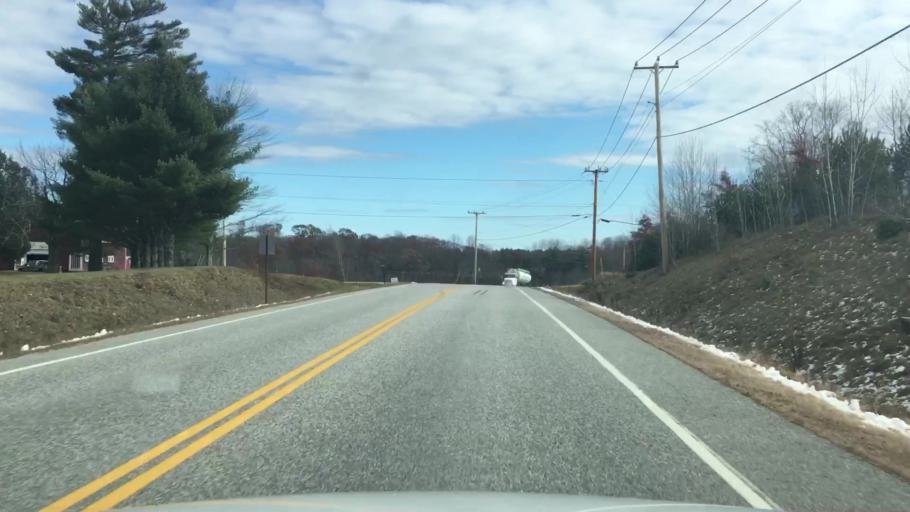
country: US
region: Maine
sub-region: Androscoggin County
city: Leeds
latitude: 44.3459
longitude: -70.1553
